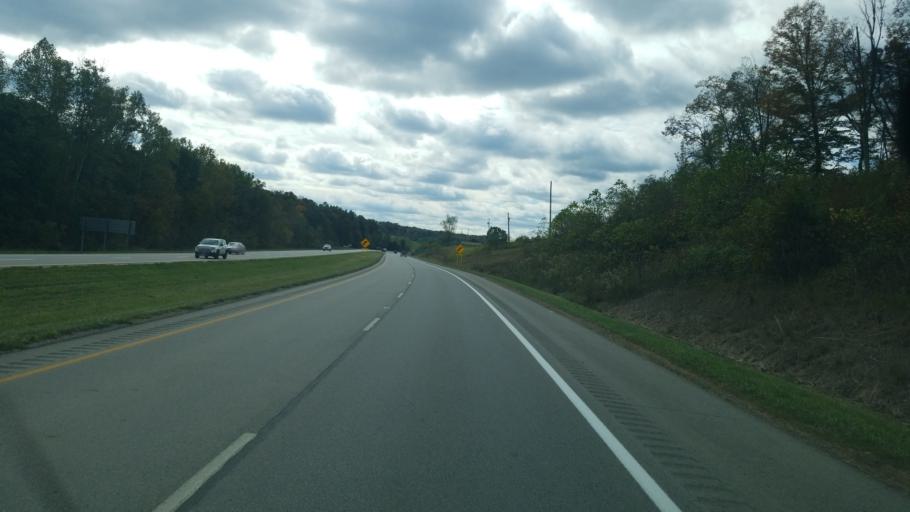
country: US
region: Ohio
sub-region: Jackson County
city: Jackson
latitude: 39.0599
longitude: -82.5882
